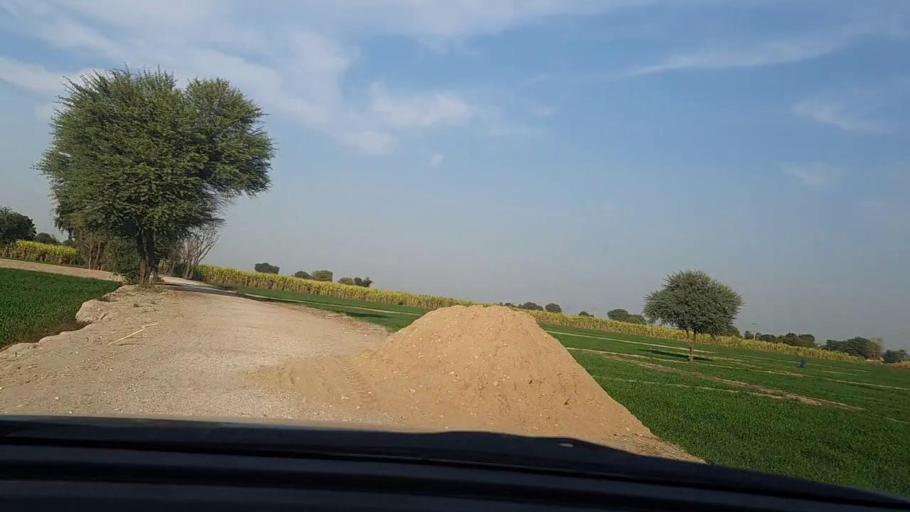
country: PK
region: Sindh
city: Daulatpur
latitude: 26.3318
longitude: 68.0289
